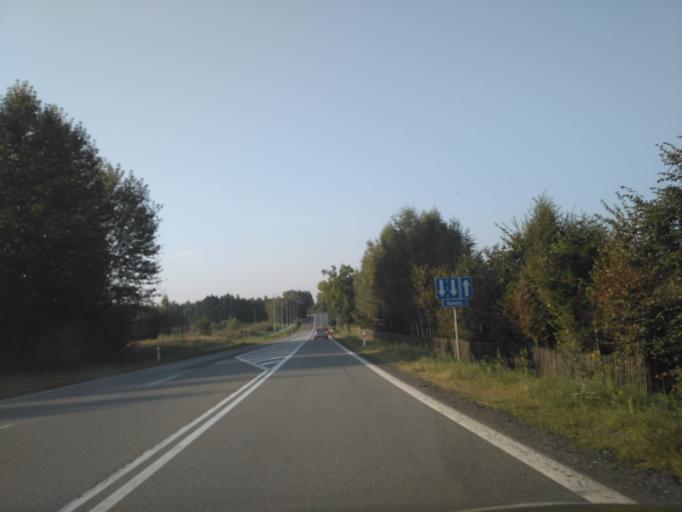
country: PL
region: Lublin Voivodeship
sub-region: Powiat janowski
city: Modliborzyce
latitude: 50.7624
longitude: 22.3222
